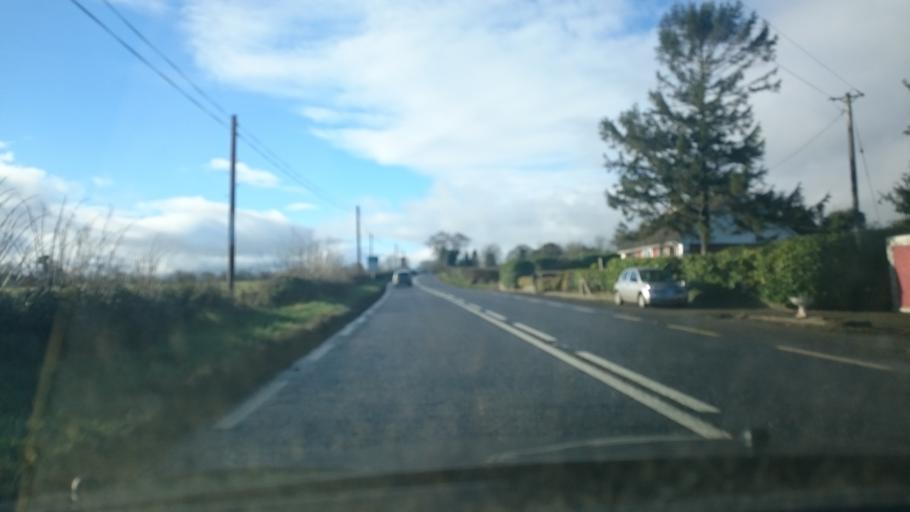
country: IE
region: Leinster
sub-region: Kilkenny
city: Callan
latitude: 52.5770
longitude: -7.3256
